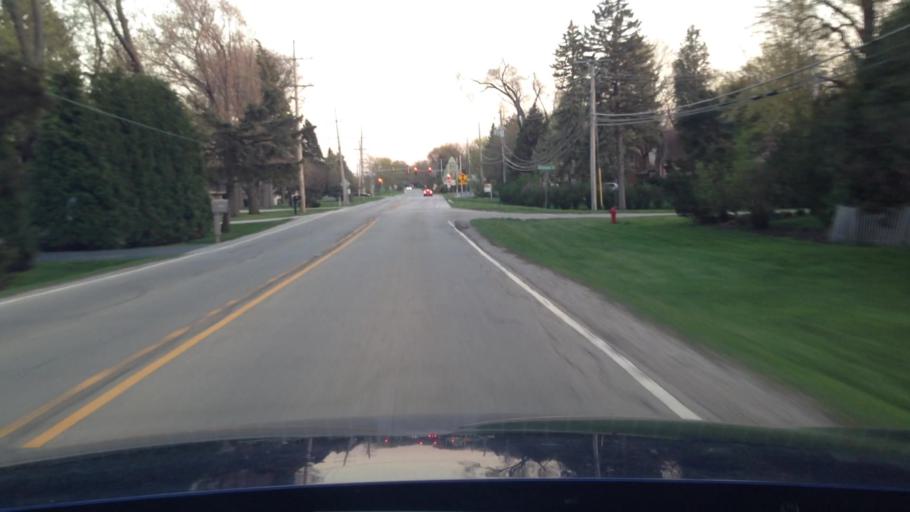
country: US
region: Illinois
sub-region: Cook County
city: Prospect Heights
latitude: 42.0976
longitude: -87.9272
